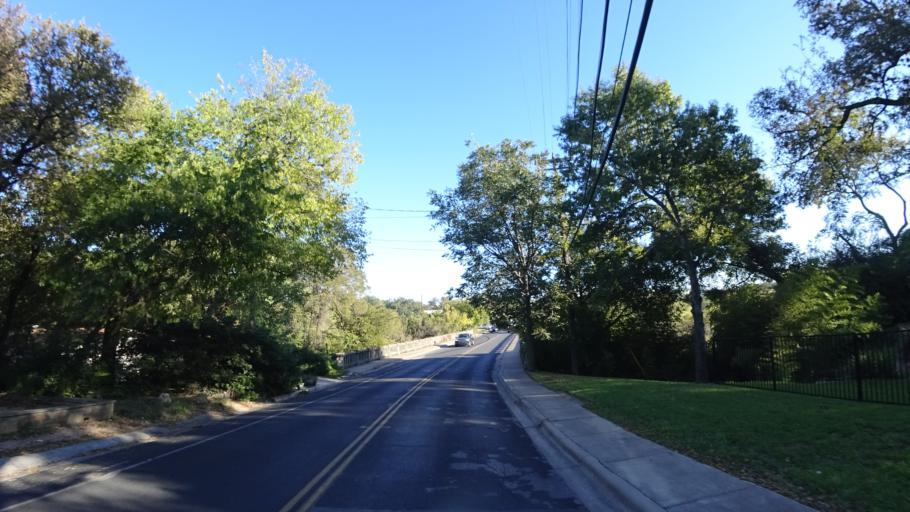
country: US
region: Texas
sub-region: Travis County
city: Austin
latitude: 30.2992
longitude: -97.7495
